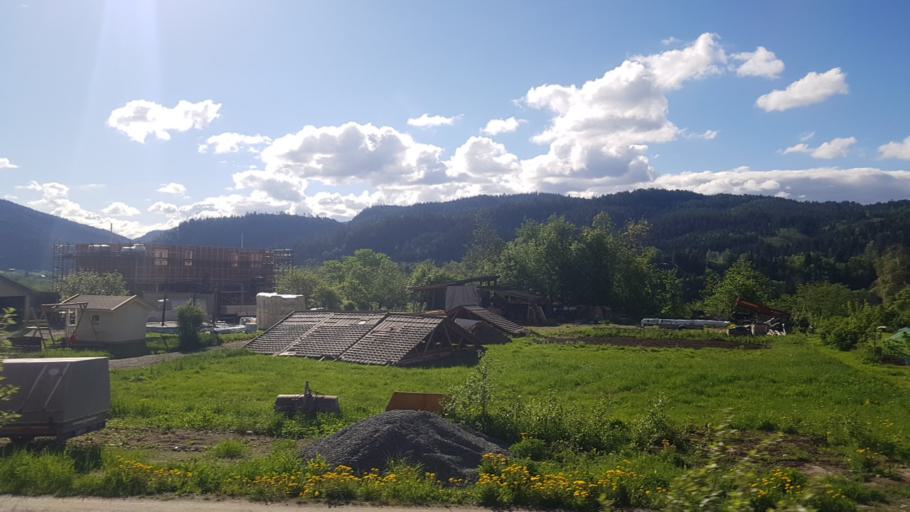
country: NO
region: Sor-Trondelag
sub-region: Midtre Gauldal
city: Storen
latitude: 63.0308
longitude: 10.2731
